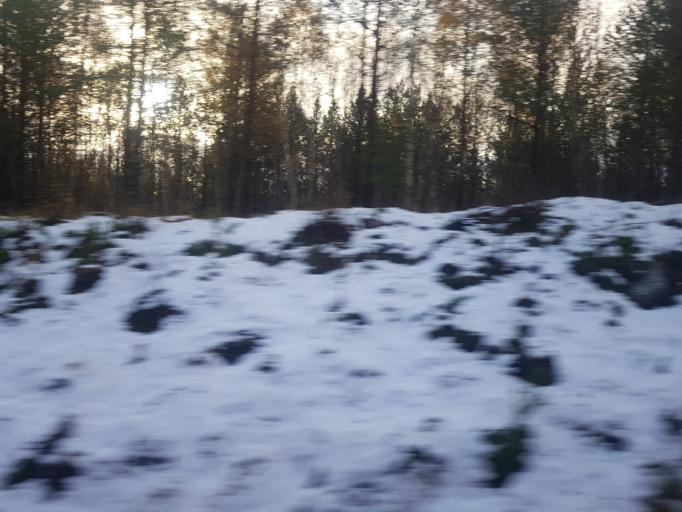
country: NO
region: Sor-Trondelag
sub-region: Oppdal
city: Oppdal
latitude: 62.6408
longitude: 9.8128
